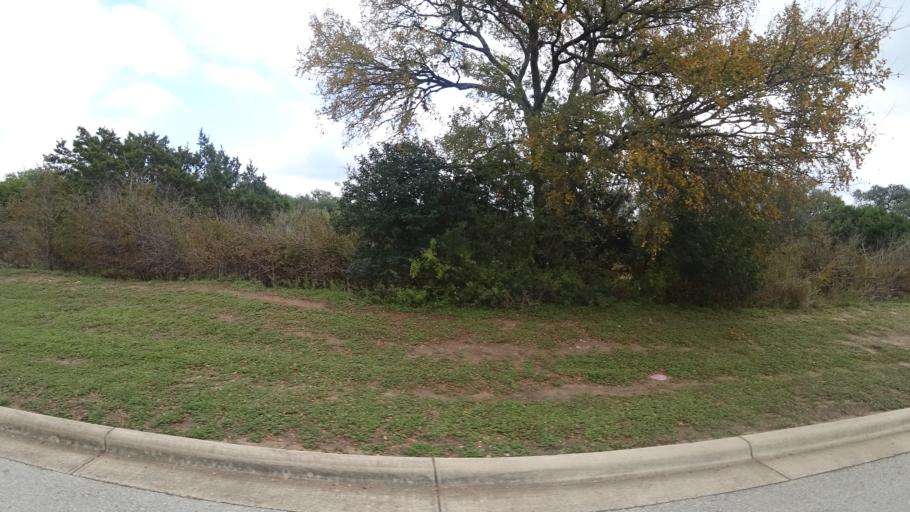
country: US
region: Texas
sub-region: Travis County
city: Bee Cave
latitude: 30.3094
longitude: -97.9041
